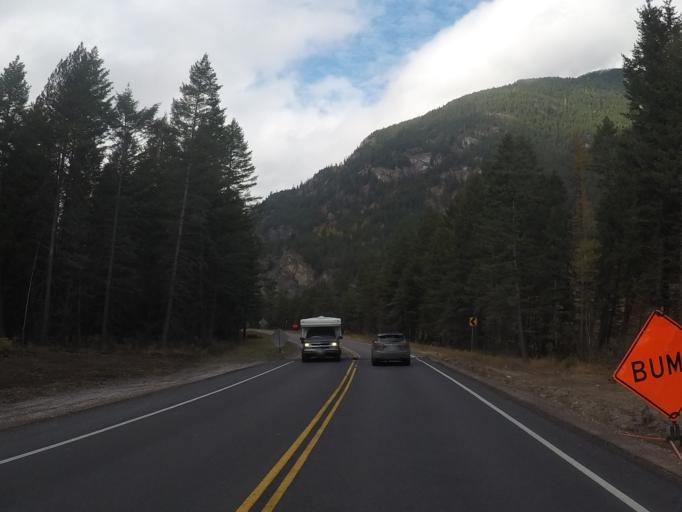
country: US
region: Montana
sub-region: Flathead County
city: Columbia Falls
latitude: 48.3879
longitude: -114.0910
